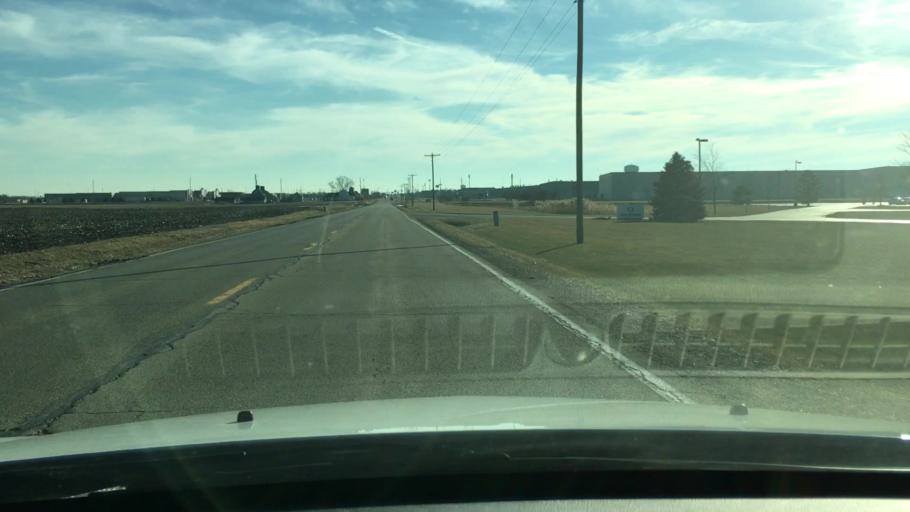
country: US
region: Illinois
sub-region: LaSalle County
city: Peru
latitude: 41.3813
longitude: -89.1257
